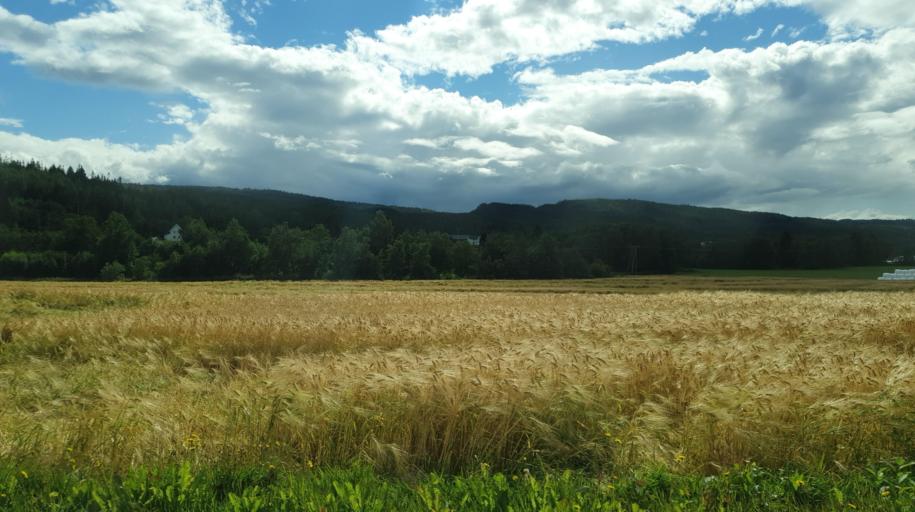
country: NO
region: Nord-Trondelag
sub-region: Levanger
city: Skogn
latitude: 63.6164
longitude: 11.2803
